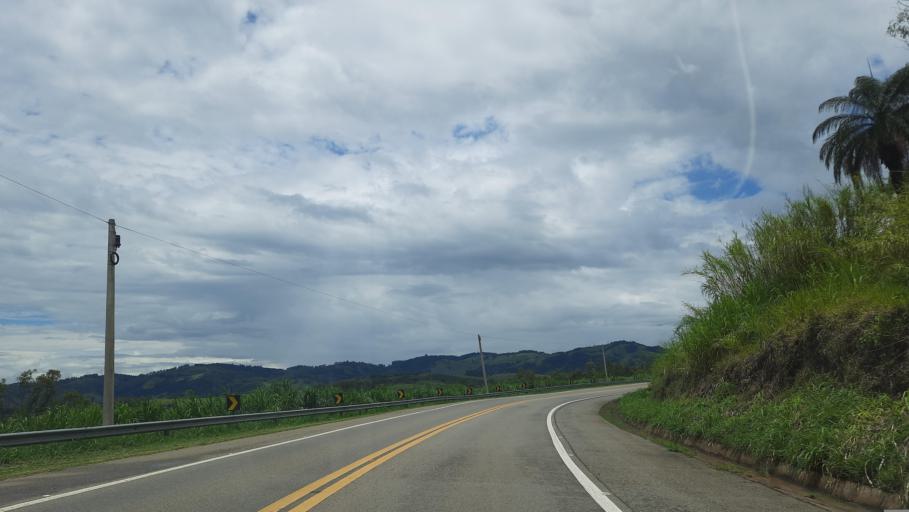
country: BR
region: Sao Paulo
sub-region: Vargem Grande Do Sul
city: Vargem Grande do Sul
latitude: -21.7992
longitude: -46.8145
